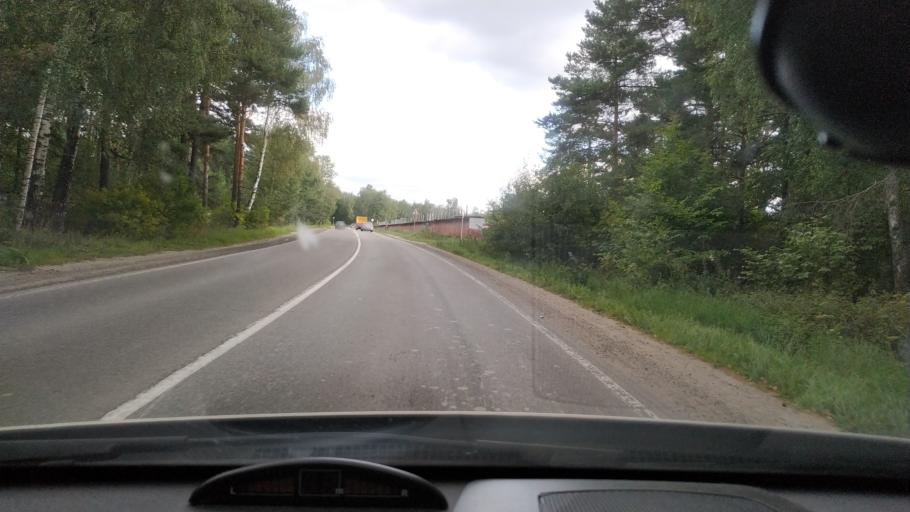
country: RU
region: Moskovskaya
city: Chornaya
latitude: 55.7659
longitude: 38.0664
